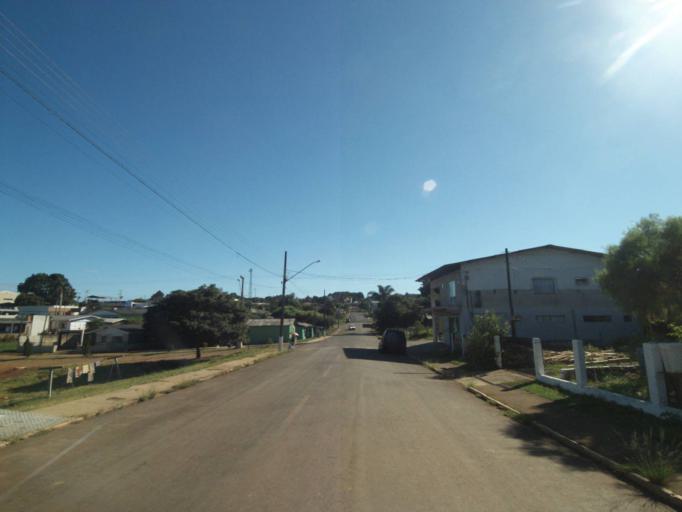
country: BR
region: Parana
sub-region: Pinhao
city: Pinhao
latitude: -25.8383
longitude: -52.0290
